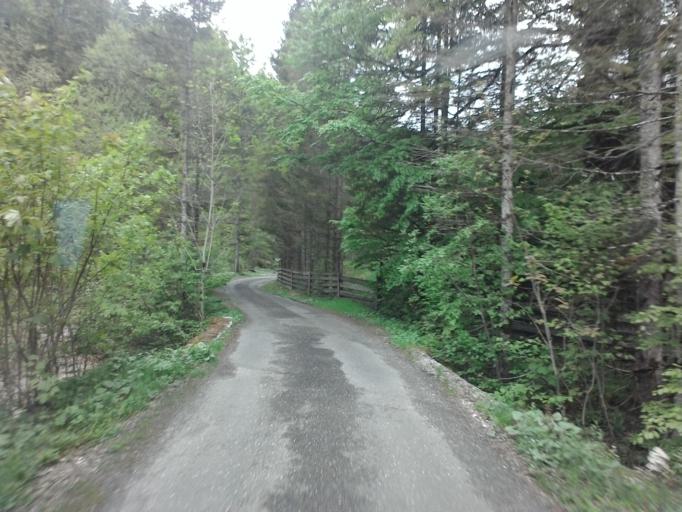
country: AT
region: Styria
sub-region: Politischer Bezirk Liezen
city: Wildalpen
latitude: 47.7049
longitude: 15.0051
